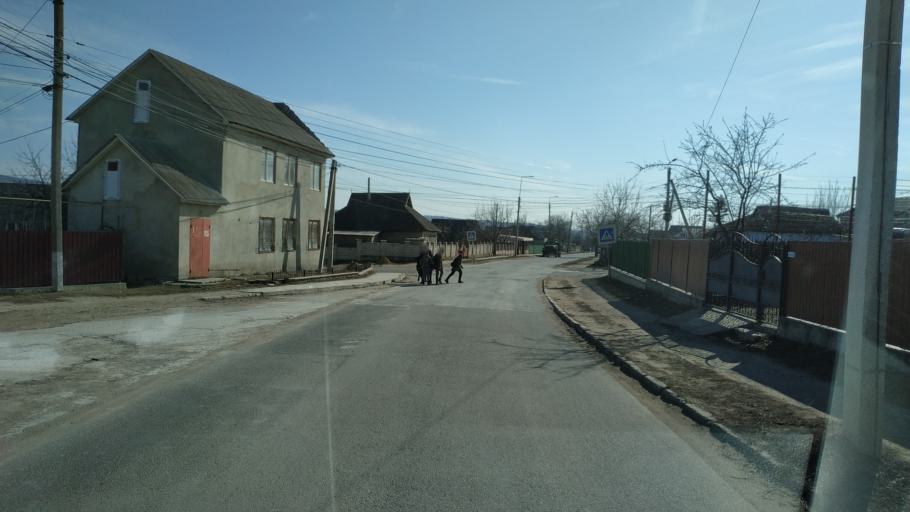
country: MD
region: Nisporeni
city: Nisporeni
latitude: 47.0760
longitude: 28.1694
